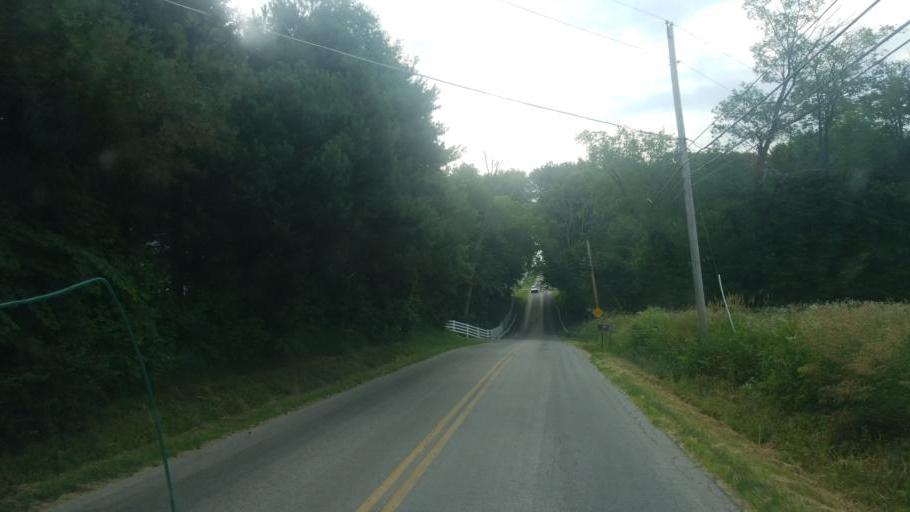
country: US
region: Ohio
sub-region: Wayne County
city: Wooster
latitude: 40.7847
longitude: -81.9834
